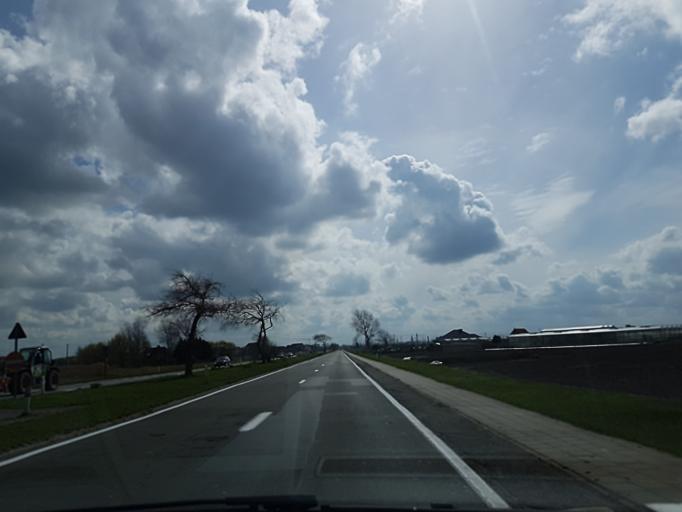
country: BE
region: Flanders
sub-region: Provincie West-Vlaanderen
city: Nieuwpoort
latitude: 51.1546
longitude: 2.7488
